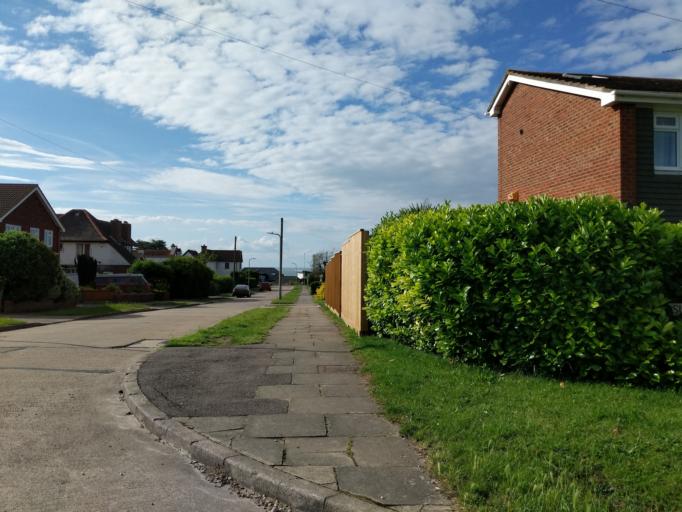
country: GB
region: England
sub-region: Kent
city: Whitstable
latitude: 51.3482
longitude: 1.0102
